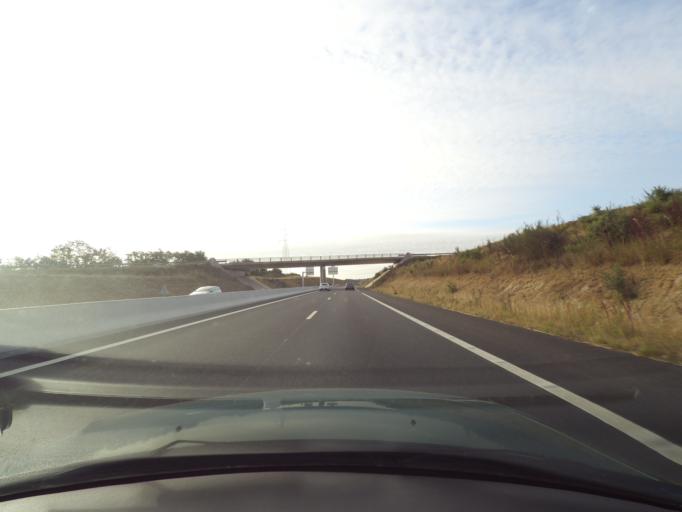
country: FR
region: Pays de la Loire
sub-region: Departement de Maine-et-Loire
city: La Tessoualle
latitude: 47.0232
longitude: -0.8829
